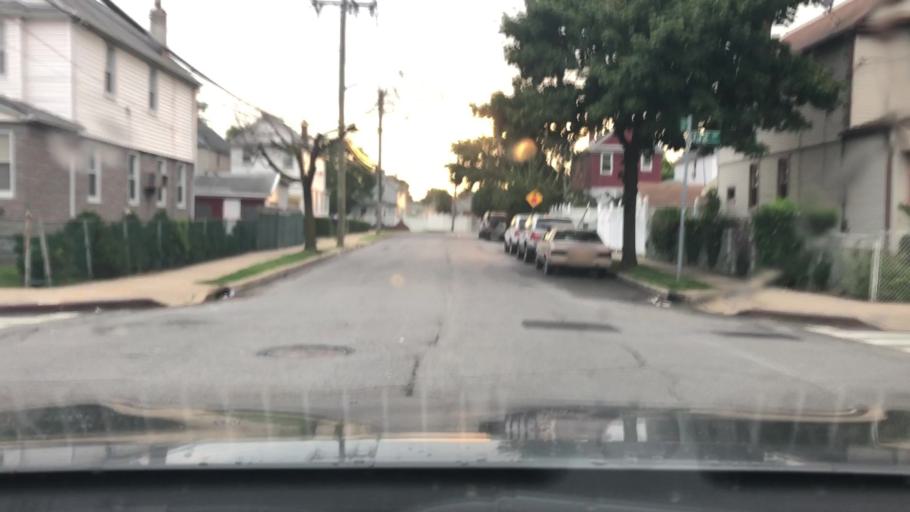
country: US
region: New York
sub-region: Queens County
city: Jamaica
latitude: 40.6693
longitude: -73.8068
